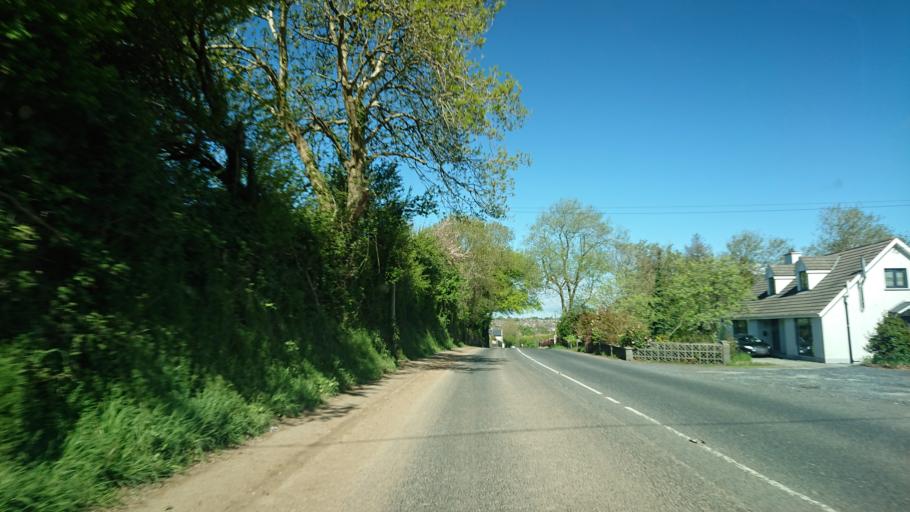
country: IE
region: Munster
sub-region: Waterford
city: Waterford
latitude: 52.2342
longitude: -7.0533
